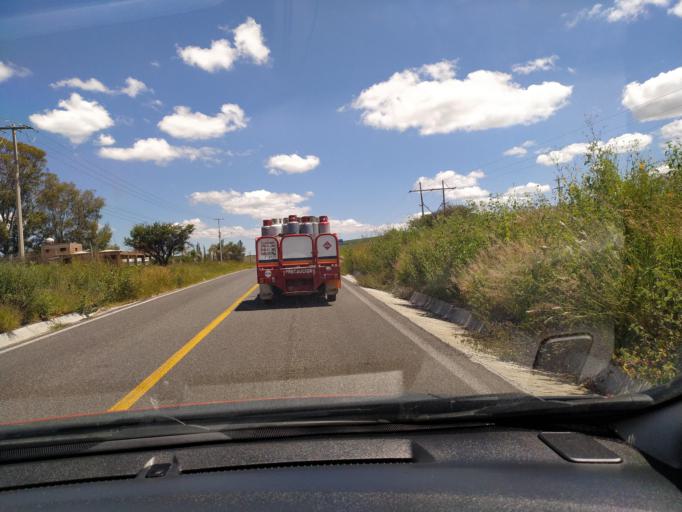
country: MX
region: Jalisco
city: San Diego de Alejandria
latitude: 21.0187
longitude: -101.9531
